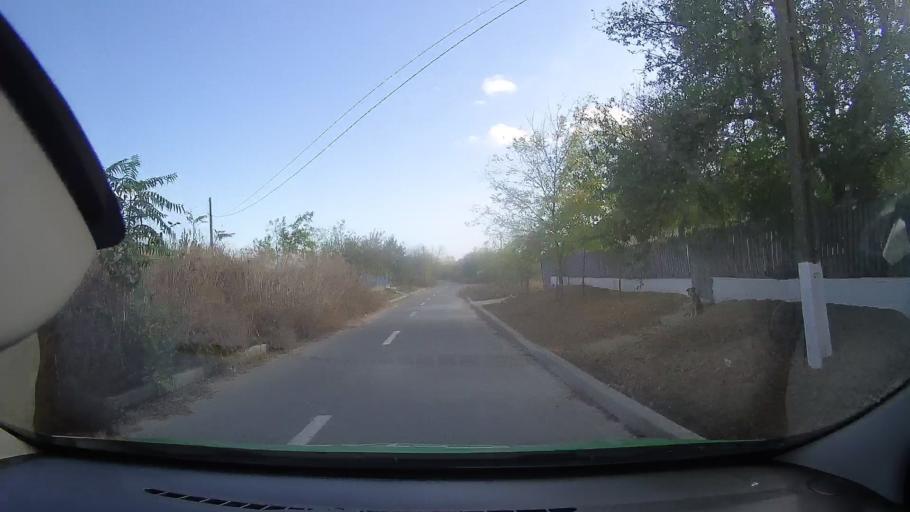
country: RO
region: Constanta
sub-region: Comuna Istria
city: Istria
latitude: 44.5775
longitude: 28.7112
